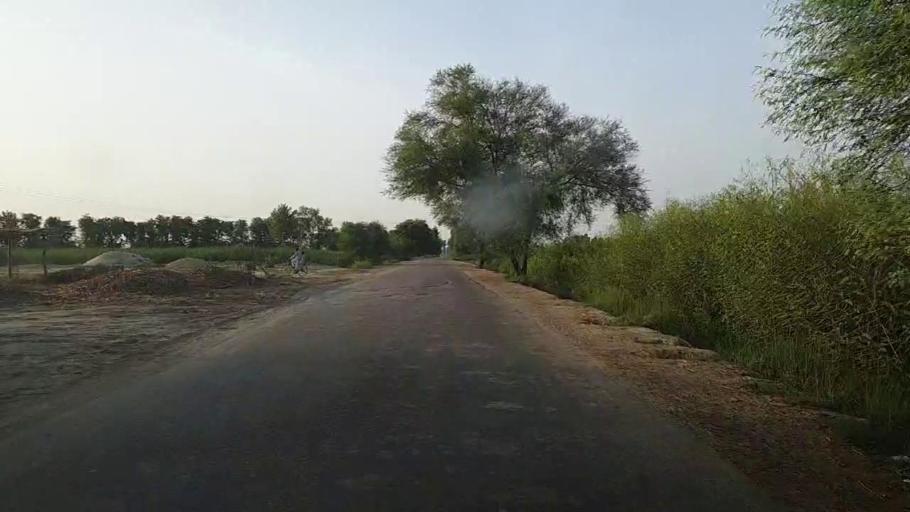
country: PK
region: Sindh
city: Ubauro
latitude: 28.1800
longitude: 69.8288
